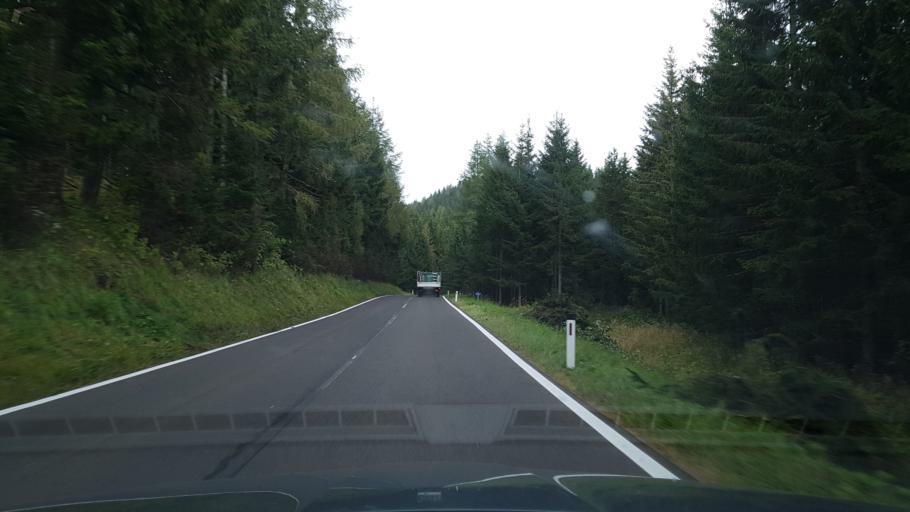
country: AT
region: Styria
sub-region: Politischer Bezirk Voitsberg
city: Salla
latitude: 47.1174
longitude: 14.9056
